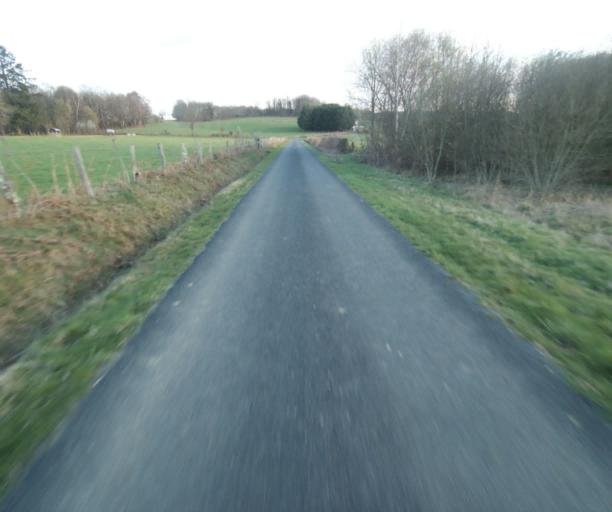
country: FR
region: Limousin
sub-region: Departement de la Correze
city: Uzerche
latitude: 45.3670
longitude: 1.5975
